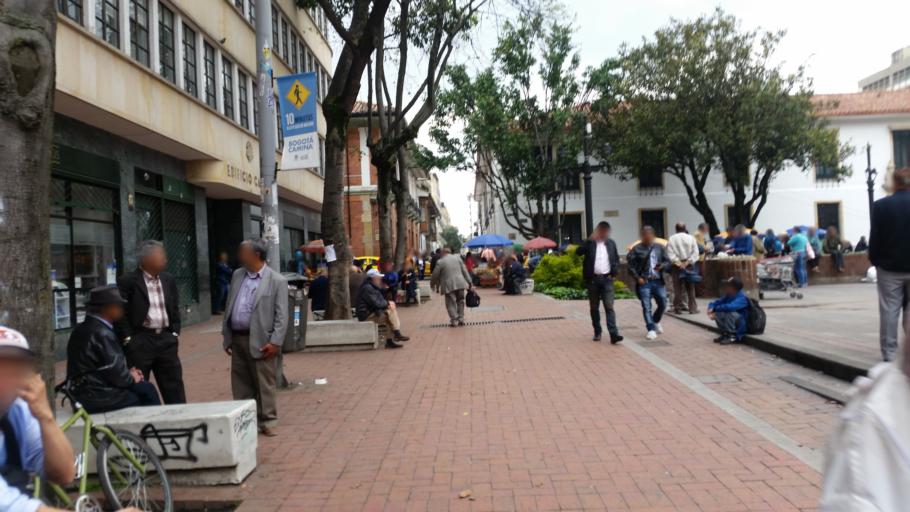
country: CO
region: Bogota D.C.
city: Bogota
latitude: 4.6007
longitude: -74.0727
